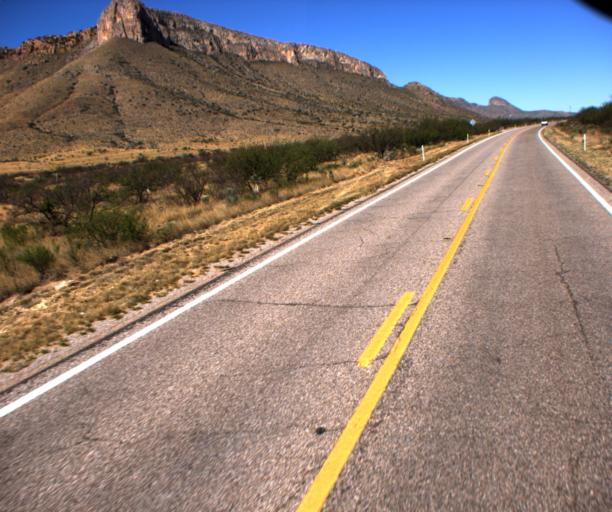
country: US
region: Arizona
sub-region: Cochise County
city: Huachuca City
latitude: 31.6949
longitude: -110.4164
